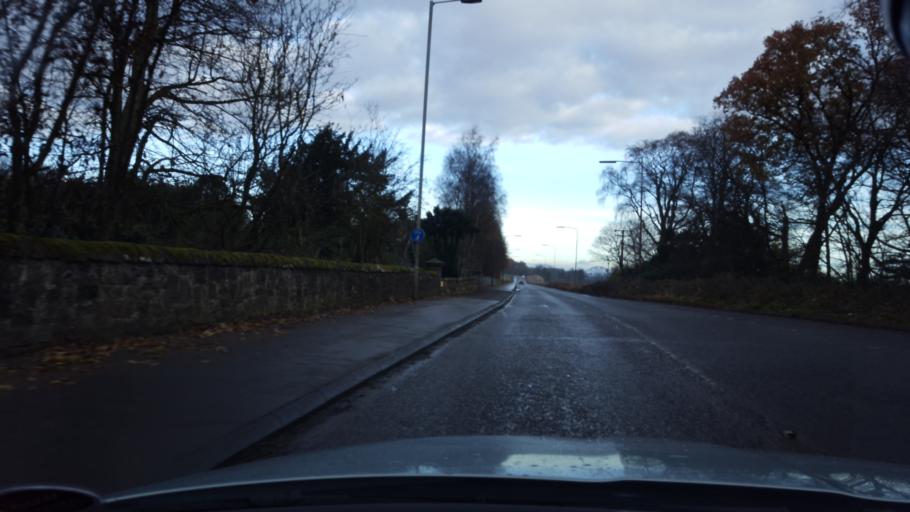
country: GB
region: Scotland
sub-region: Edinburgh
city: Kirkliston
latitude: 55.9654
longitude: -3.4023
